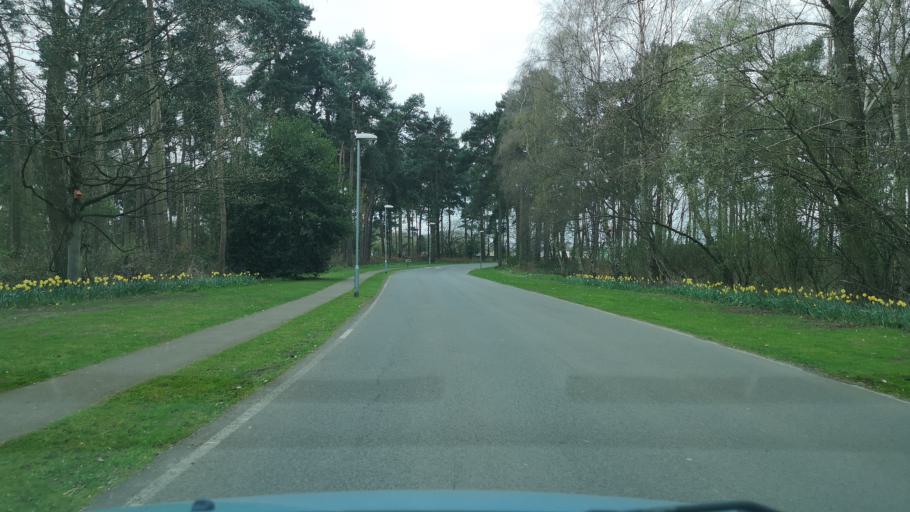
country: GB
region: England
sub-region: North Lincolnshire
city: Scunthorpe
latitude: 53.5701
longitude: -0.6832
